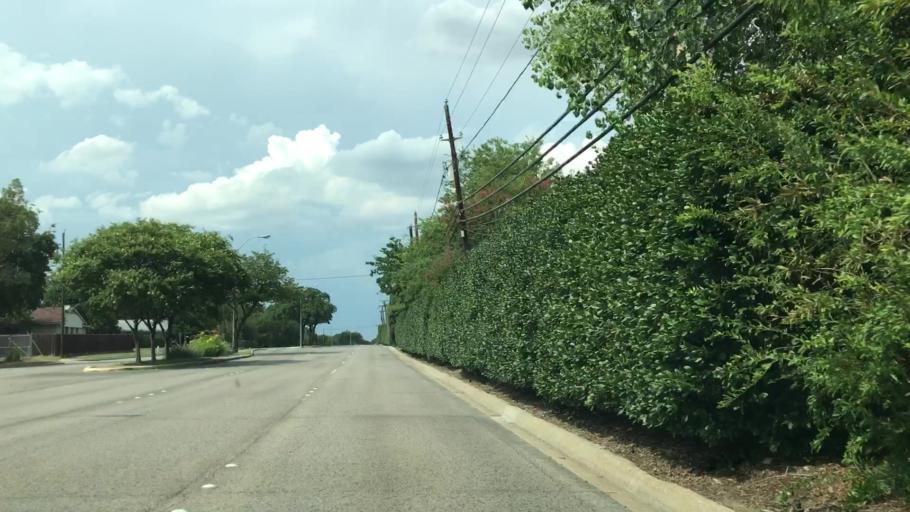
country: US
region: Texas
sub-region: Dallas County
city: Carrollton
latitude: 32.9400
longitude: -96.8732
